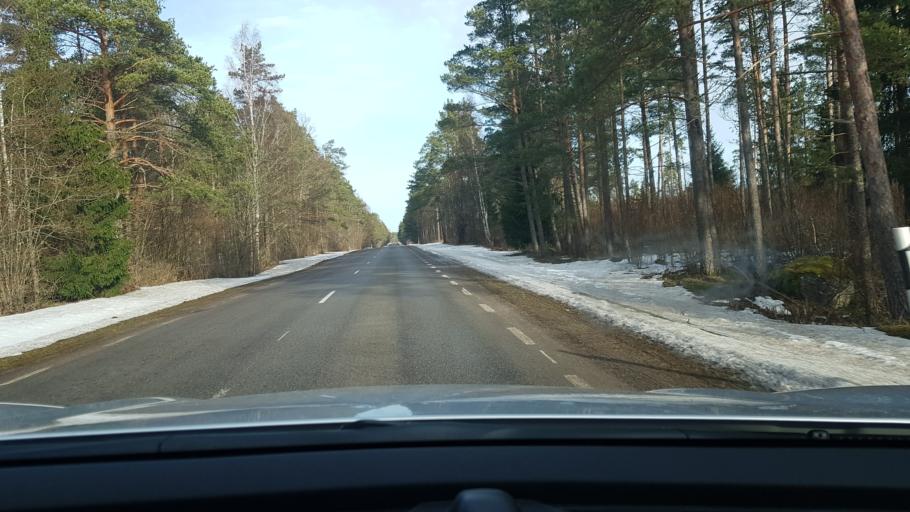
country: EE
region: Saare
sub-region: Kuressaare linn
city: Kuressaare
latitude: 58.4685
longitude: 22.7023
